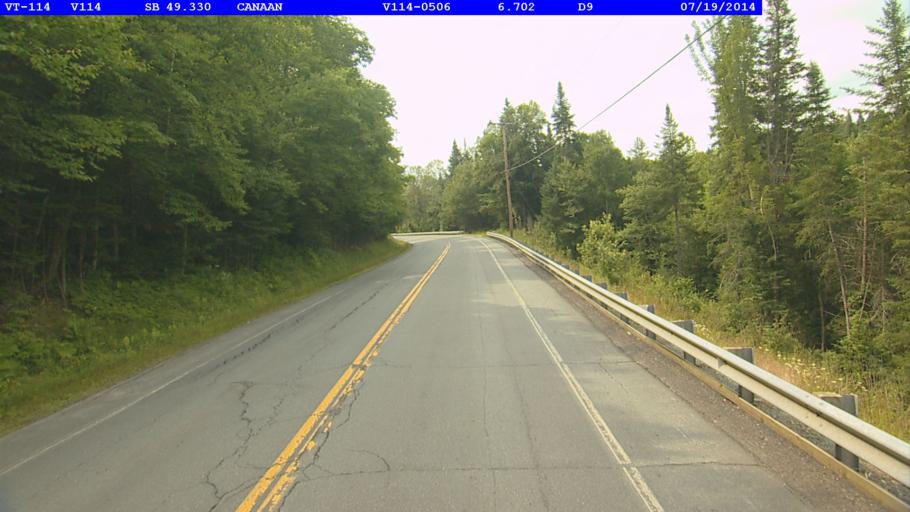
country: US
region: New Hampshire
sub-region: Coos County
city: Colebrook
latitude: 45.0086
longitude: -71.5621
